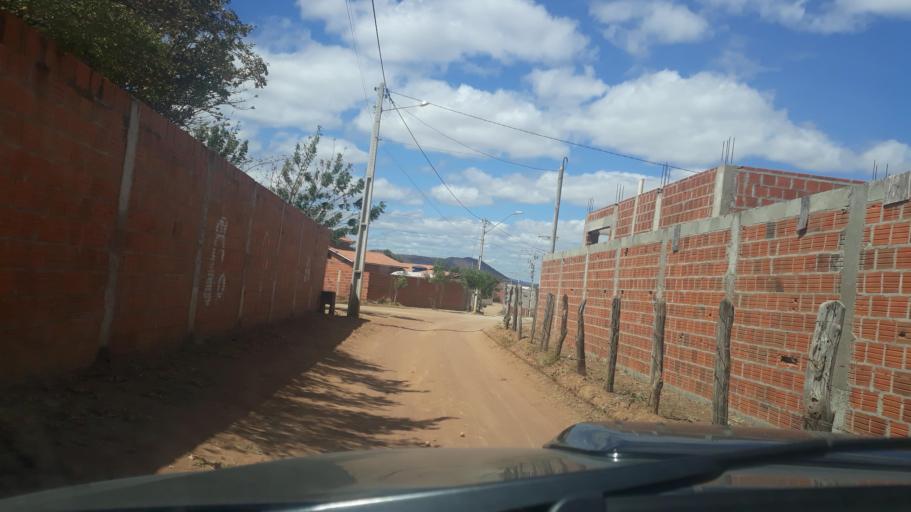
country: BR
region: Bahia
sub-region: Riacho De Santana
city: Riacho de Santana
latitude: -13.9042
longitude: -42.8510
